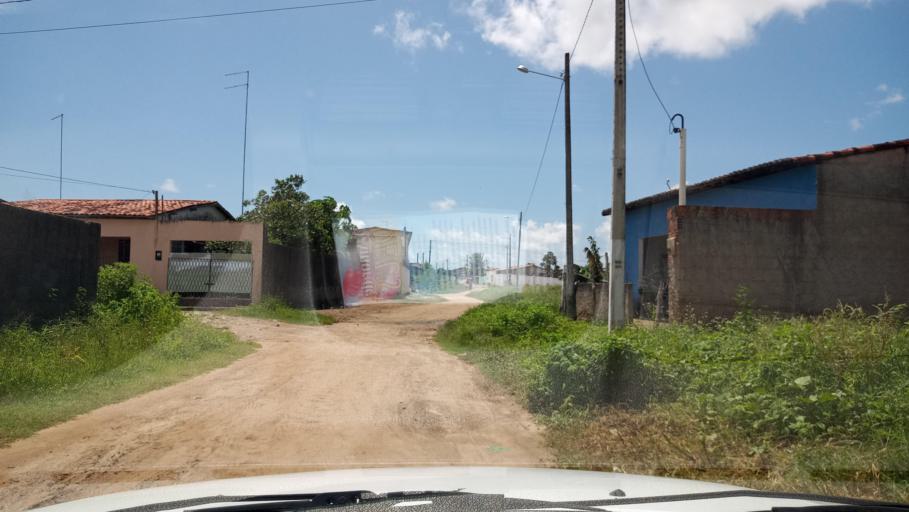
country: BR
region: Rio Grande do Norte
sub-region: Goianinha
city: Goianinha
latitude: -6.2570
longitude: -35.2068
